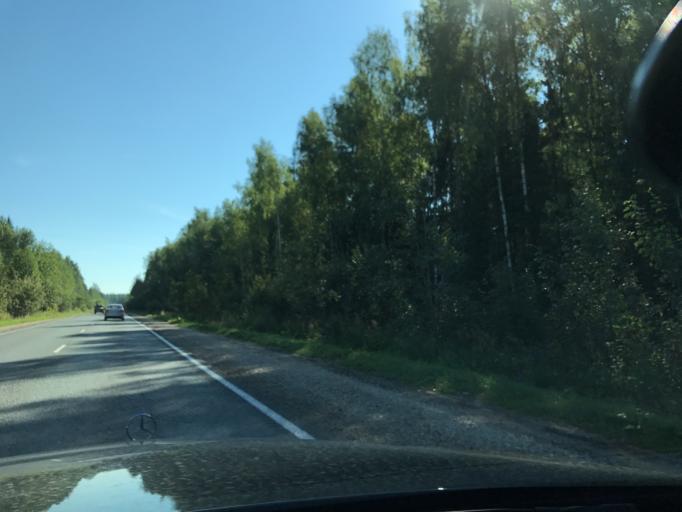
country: RU
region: Vladimir
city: Kirzhach
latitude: 56.1117
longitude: 38.7308
